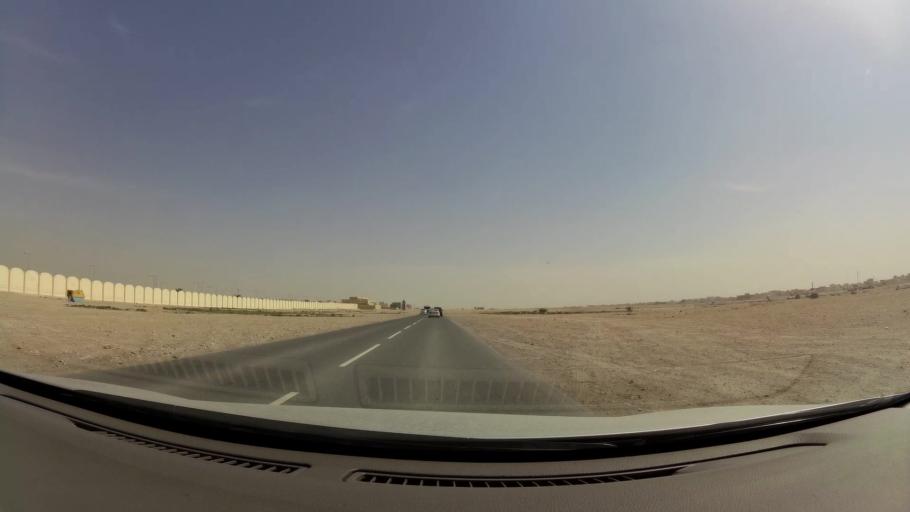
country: QA
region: Baladiyat ar Rayyan
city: Ar Rayyan
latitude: 25.2570
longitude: 51.3837
